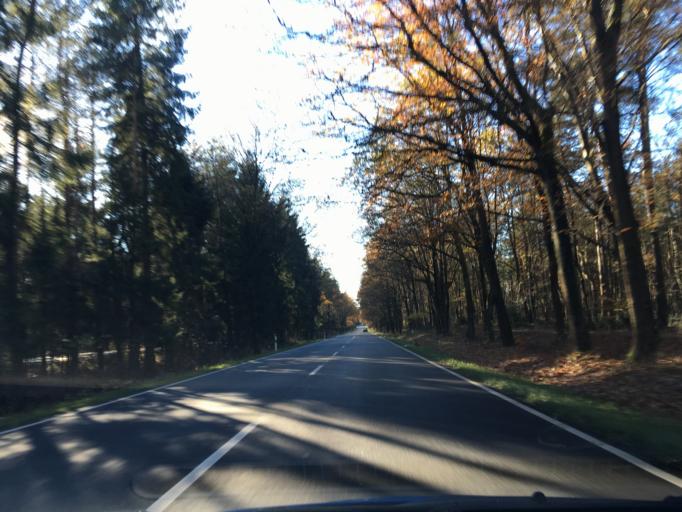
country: DE
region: Lower Saxony
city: Bispingen
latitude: 53.0614
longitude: 10.0375
